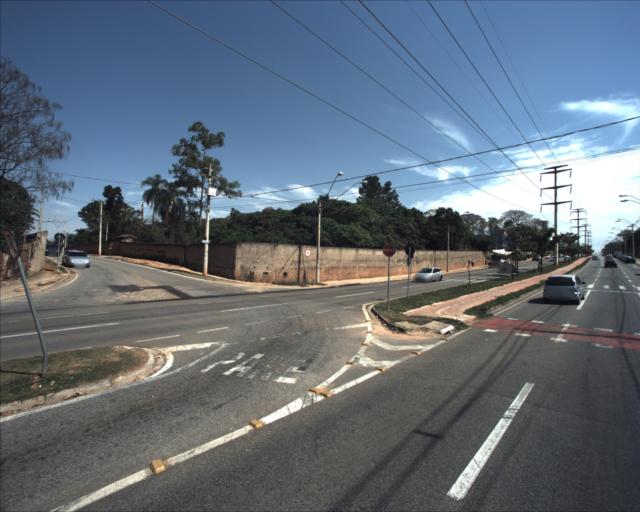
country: BR
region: Sao Paulo
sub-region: Sorocaba
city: Sorocaba
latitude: -23.4459
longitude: -47.4980
